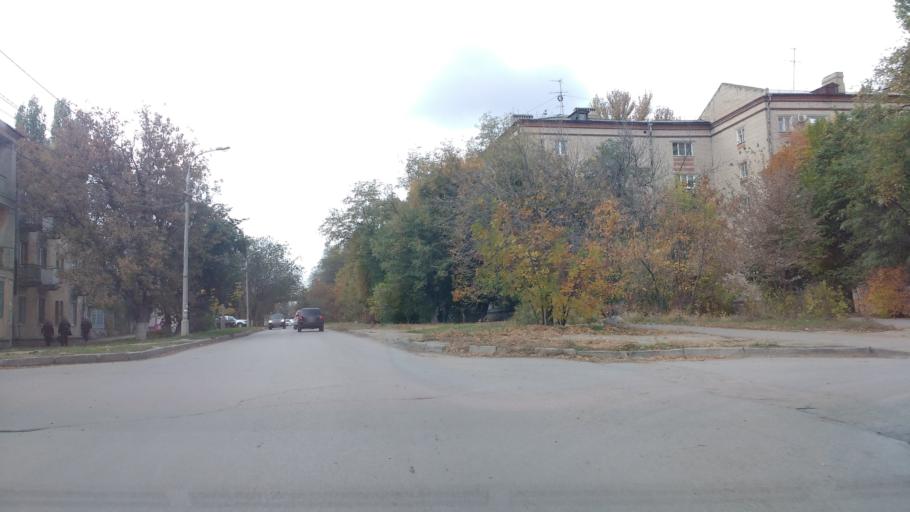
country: RU
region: Volgograd
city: Vodstroy
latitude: 48.7738
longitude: 44.5486
